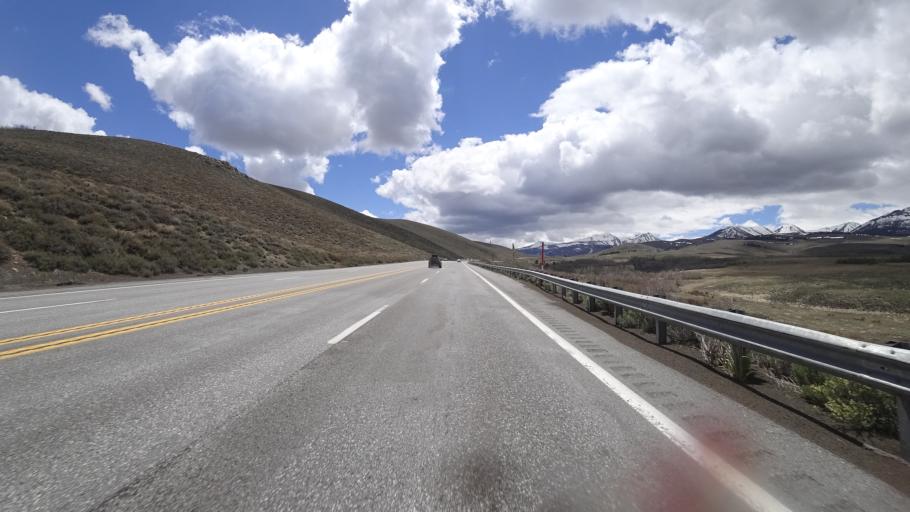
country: US
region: California
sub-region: Mono County
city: Bridgeport
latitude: 38.1104
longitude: -119.1777
